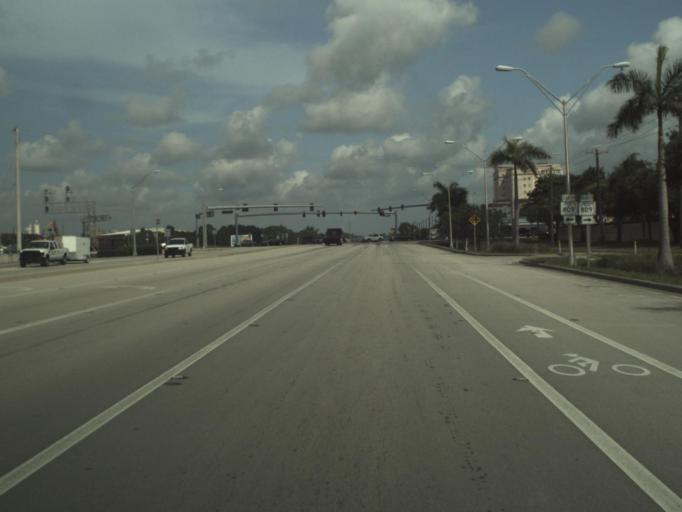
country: US
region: Florida
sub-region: Palm Beach County
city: Mangonia Park
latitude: 26.7788
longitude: -80.1058
